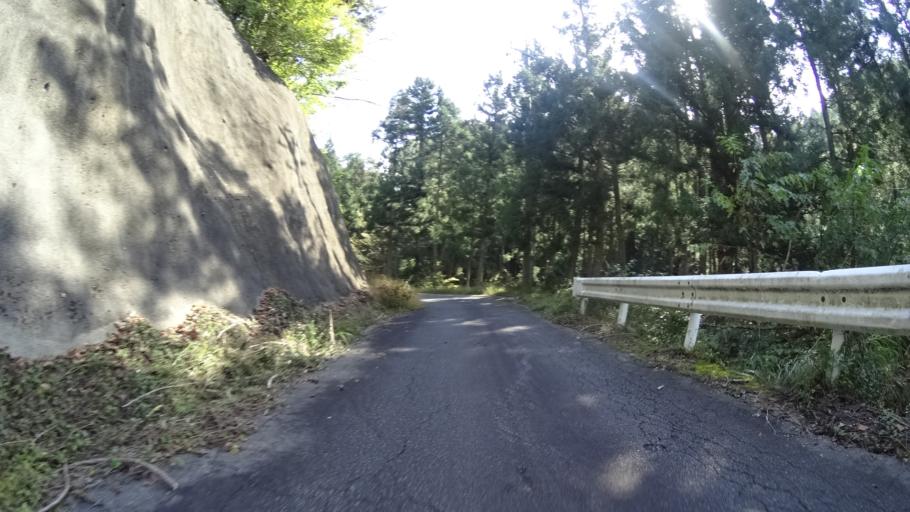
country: JP
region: Yamanashi
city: Otsuki
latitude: 35.5773
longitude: 138.9823
